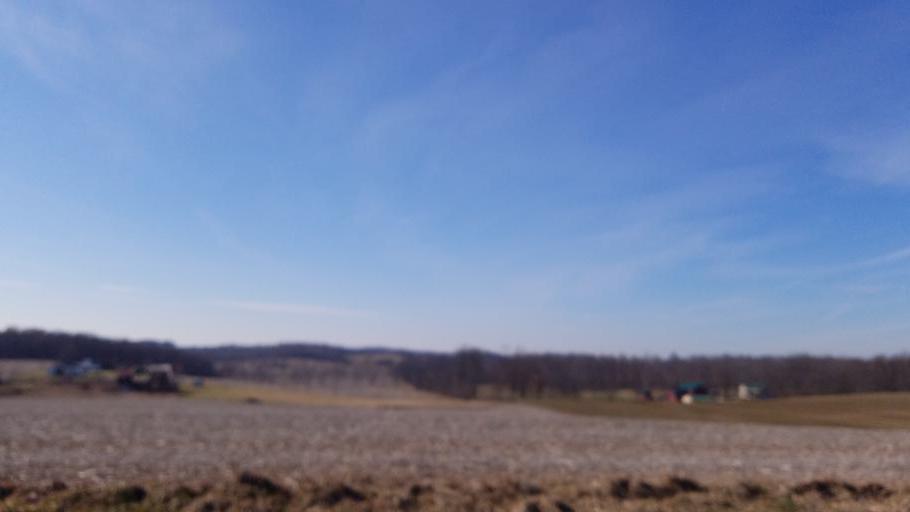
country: US
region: Ohio
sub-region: Knox County
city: Fredericktown
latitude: 40.5019
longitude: -82.4467
